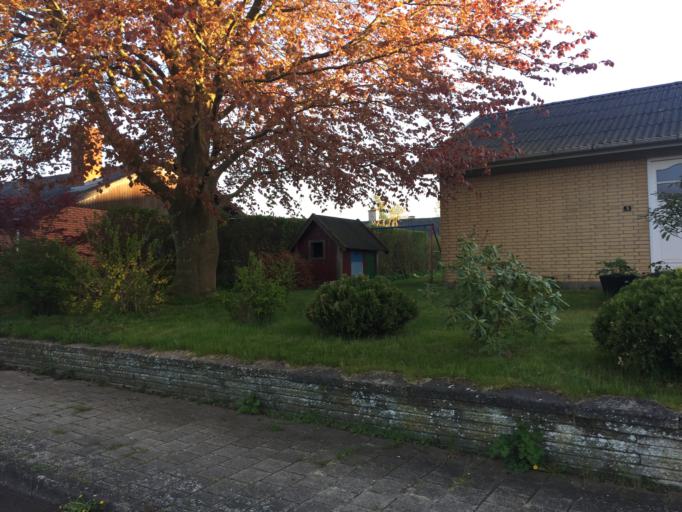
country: DK
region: Capital Region
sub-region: Hillerod Kommune
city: Hillerod
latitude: 55.9452
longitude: 12.2825
